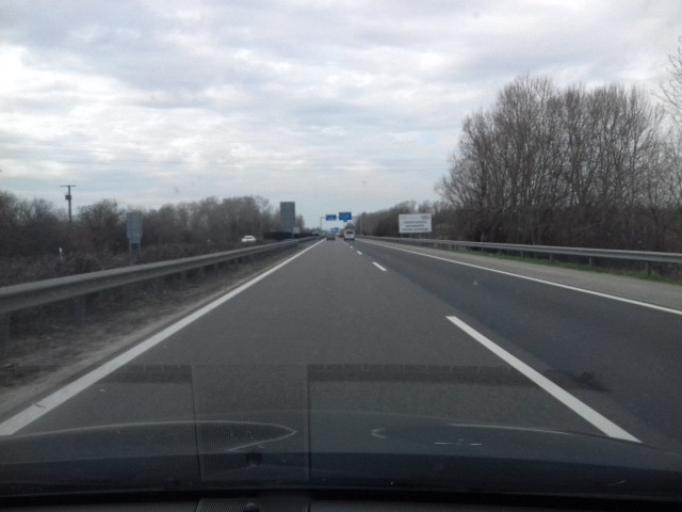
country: HU
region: Pest
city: Gyal
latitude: 47.3807
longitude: 19.1800
